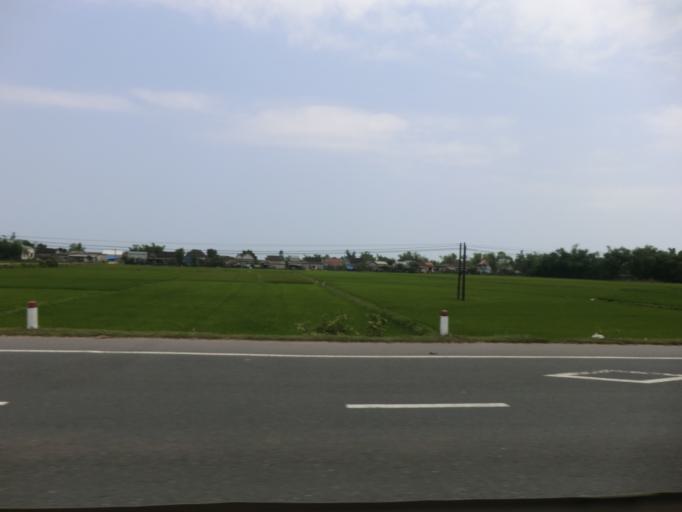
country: VN
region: Thua Thien-Hue
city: Phu Vang
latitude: 16.3579
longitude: 107.7361
